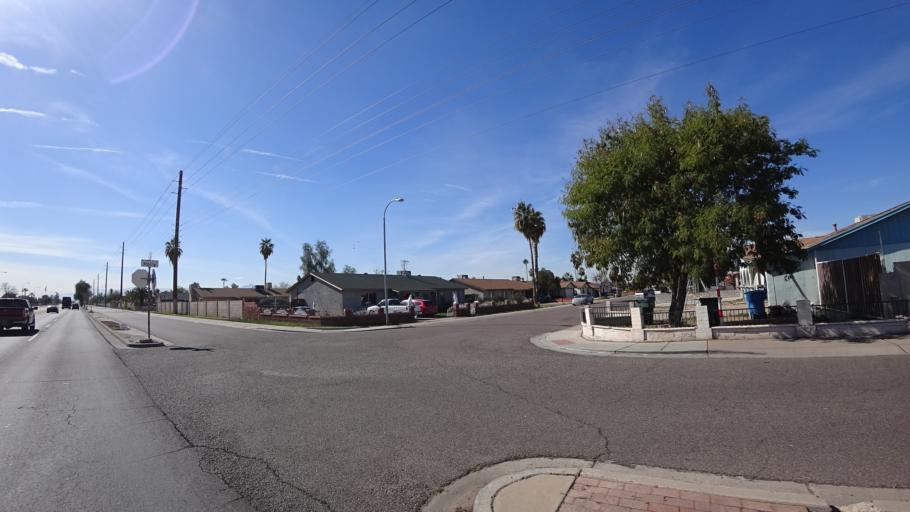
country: US
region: Arizona
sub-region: Maricopa County
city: Glendale
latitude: 33.4717
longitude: -112.1865
